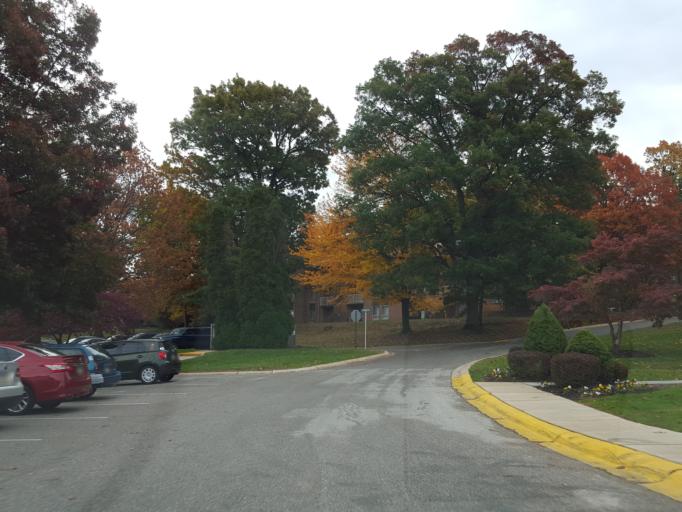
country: US
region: Pennsylvania
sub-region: York County
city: Valley View
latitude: 39.9403
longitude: -76.6900
